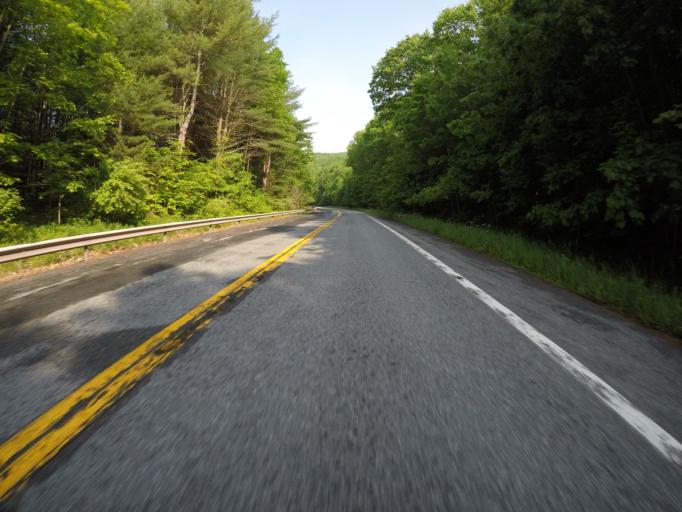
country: US
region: New York
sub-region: Sullivan County
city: Livingston Manor
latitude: 42.1267
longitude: -74.7081
